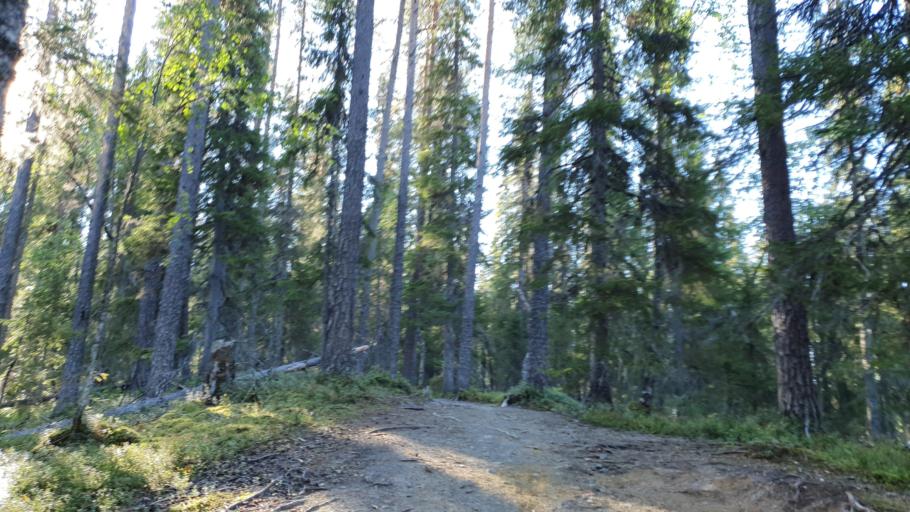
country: FI
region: Lapland
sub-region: Tunturi-Lappi
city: Kolari
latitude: 67.5967
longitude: 24.2423
